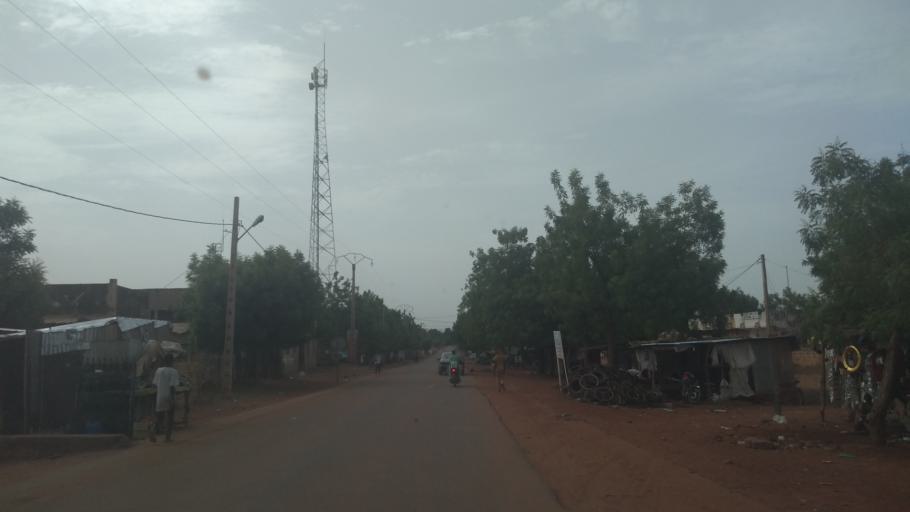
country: ML
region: Bamako
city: Bamako
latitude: 12.6162
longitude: -7.7782
